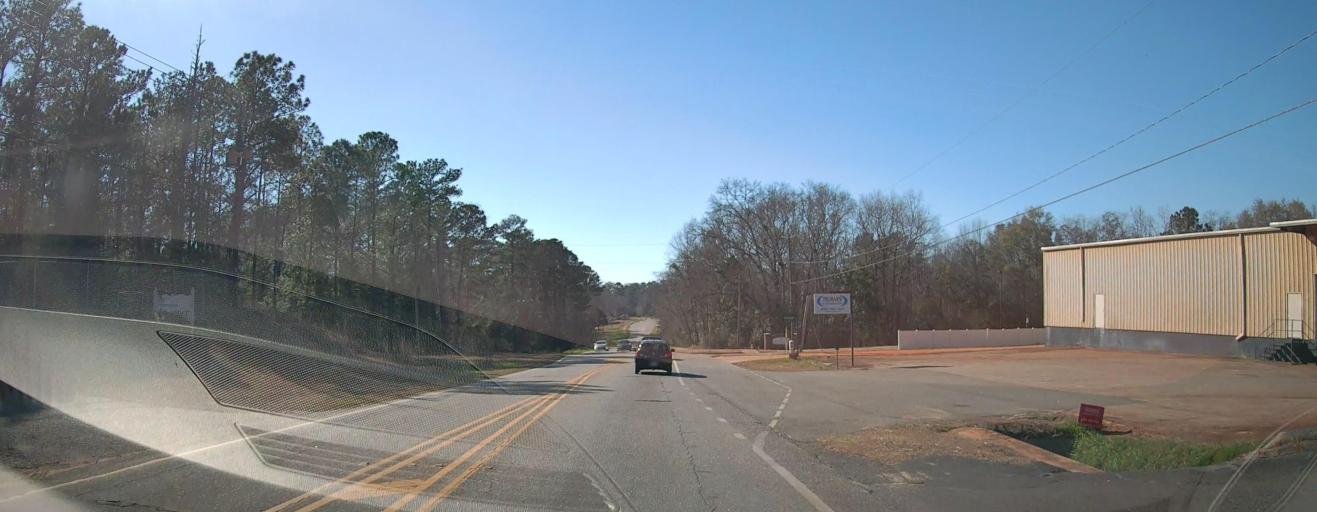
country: US
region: Georgia
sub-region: Sumter County
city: Americus
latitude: 32.0598
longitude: -84.2058
